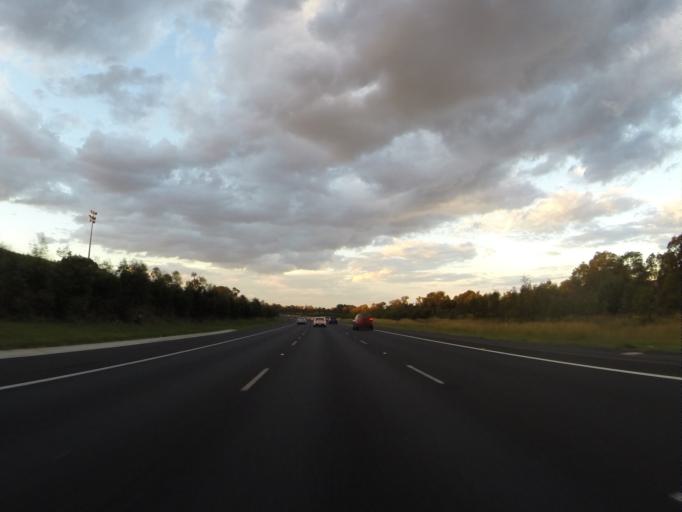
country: AU
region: New South Wales
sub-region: Campbelltown Municipality
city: Leumeah
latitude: -34.0449
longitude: 150.8195
